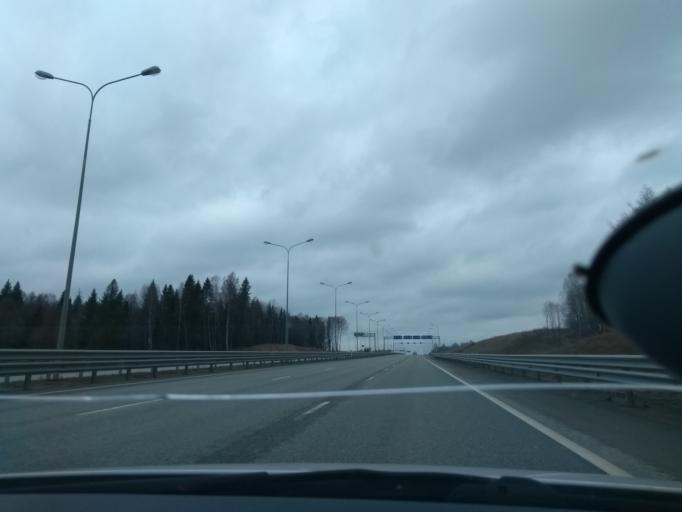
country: RU
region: Perm
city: Bershet'
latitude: 57.7308
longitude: 56.3475
